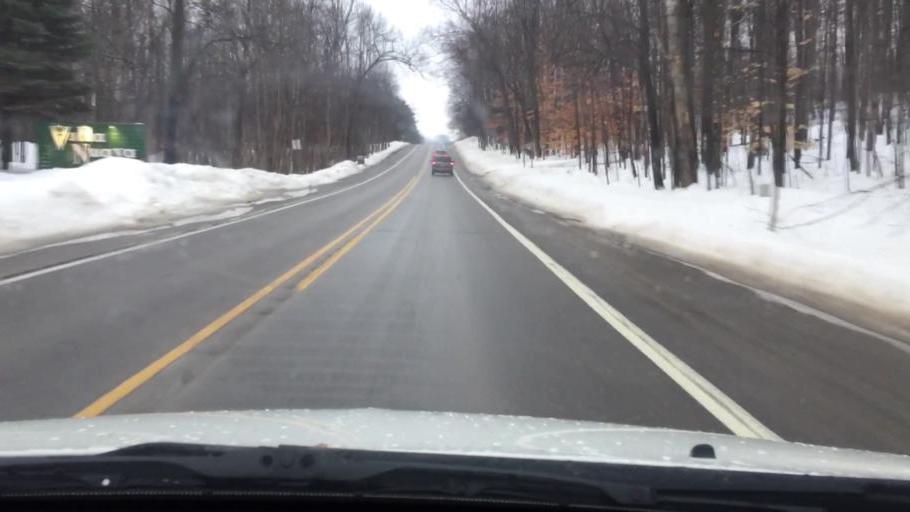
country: US
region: Michigan
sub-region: Charlevoix County
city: East Jordan
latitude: 45.2415
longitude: -85.1812
